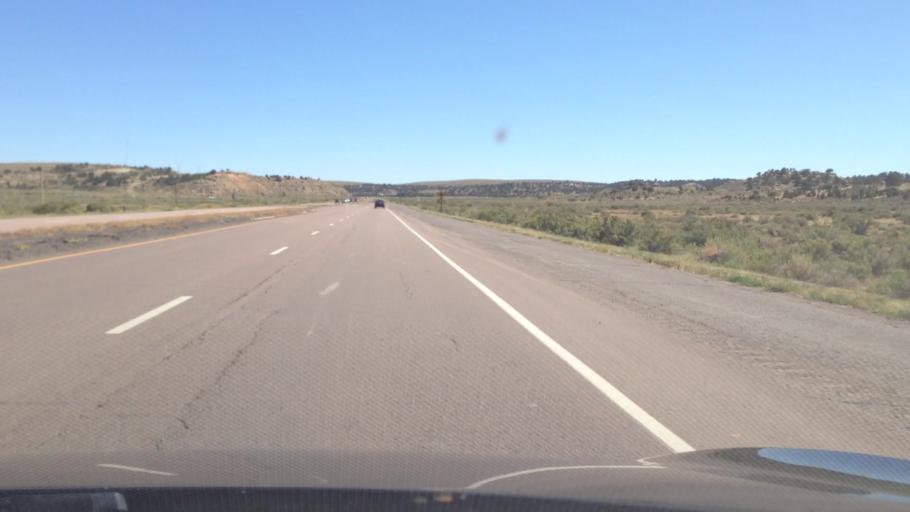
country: US
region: Arizona
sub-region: Apache County
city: Window Rock
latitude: 35.6475
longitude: -109.0329
